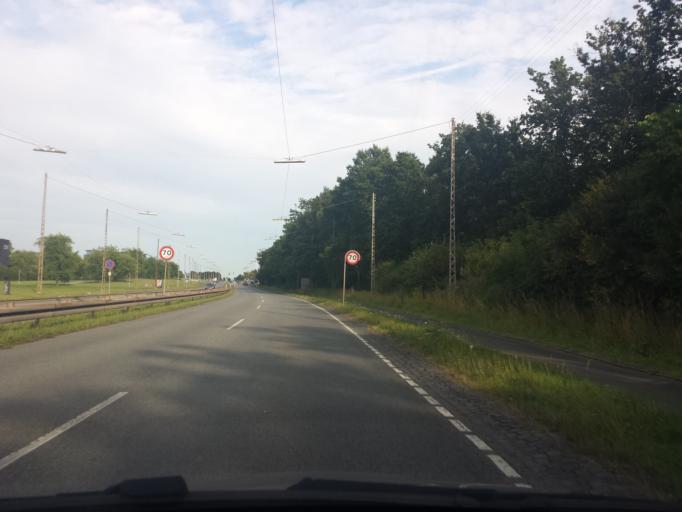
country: DK
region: Capital Region
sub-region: Ballerup Kommune
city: Ballerup
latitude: 55.7296
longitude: 12.3807
